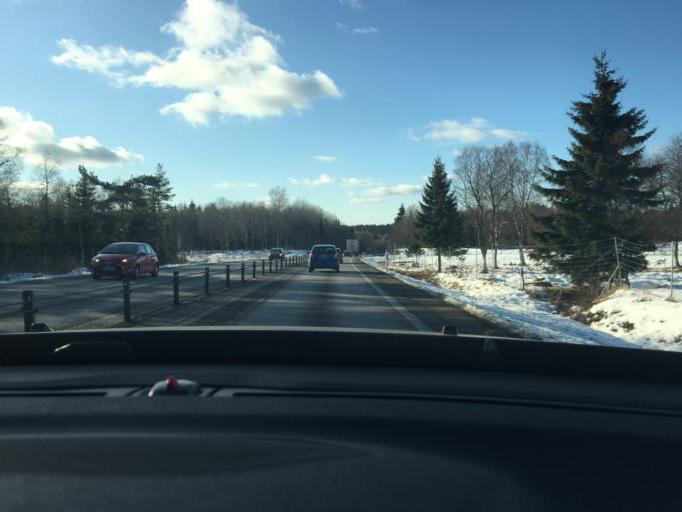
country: SE
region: Vaestra Goetaland
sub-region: Ulricehamns Kommun
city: Ulricehamn
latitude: 57.7955
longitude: 13.5497
